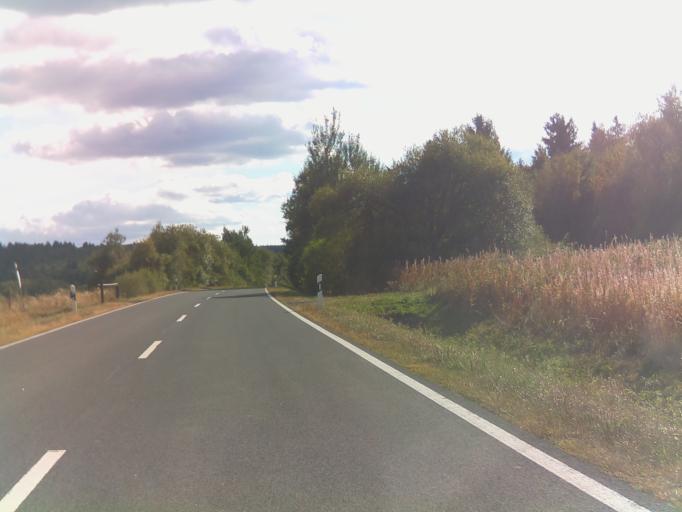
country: DE
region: Thuringia
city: Birx
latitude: 50.5127
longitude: 10.0532
